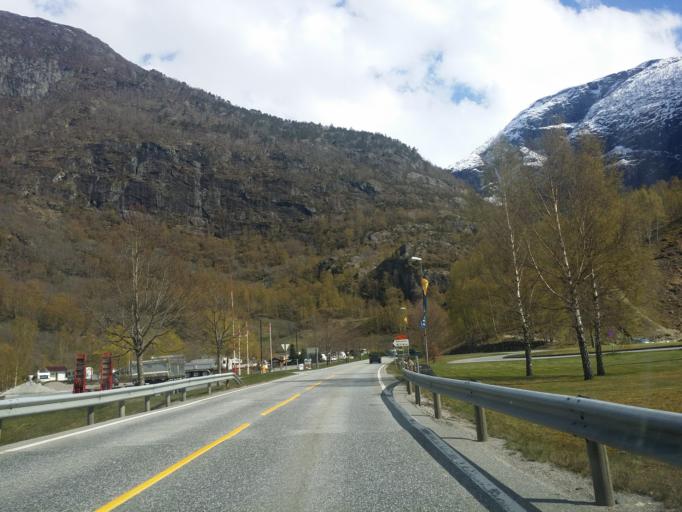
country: NO
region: Hordaland
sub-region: Eidfjord
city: Eidfjord
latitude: 60.4235
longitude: 7.1355
